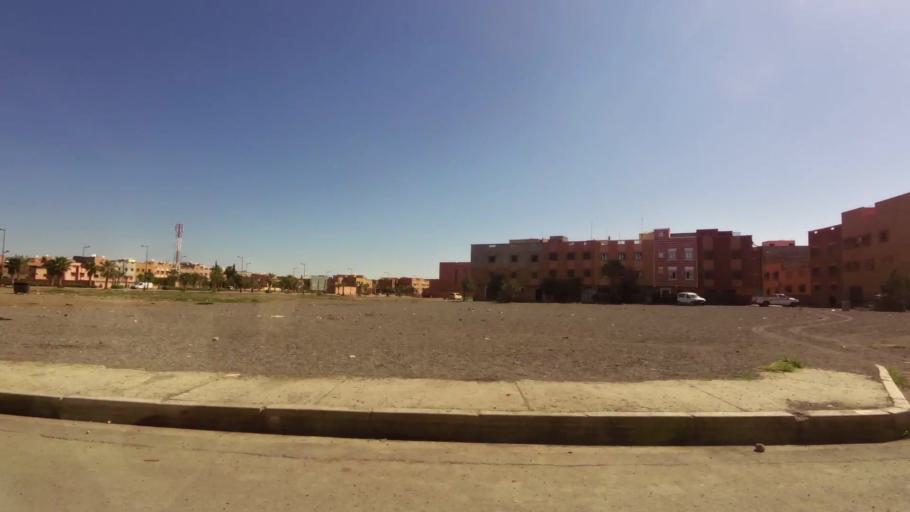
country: MA
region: Marrakech-Tensift-Al Haouz
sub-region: Marrakech
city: Marrakesh
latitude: 31.5885
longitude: -8.0551
